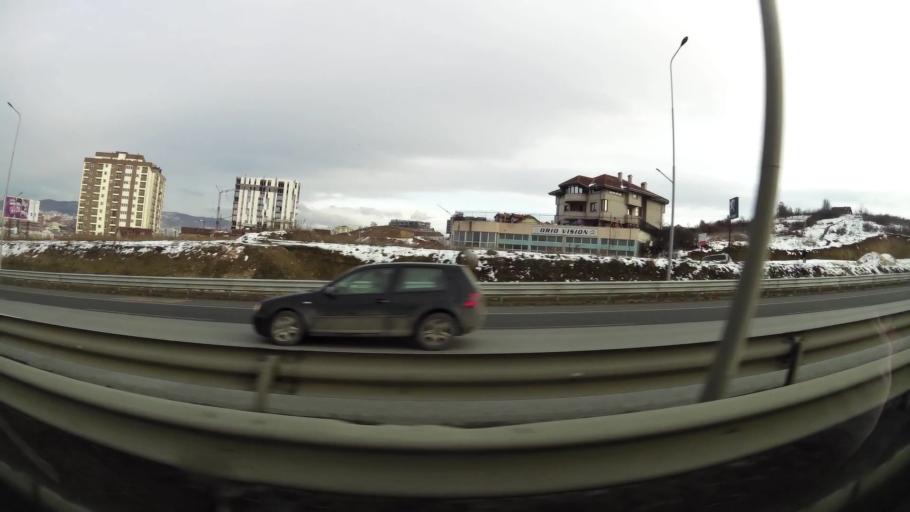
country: XK
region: Pristina
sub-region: Komuna e Prishtines
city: Pristina
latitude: 42.6397
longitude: 21.1545
